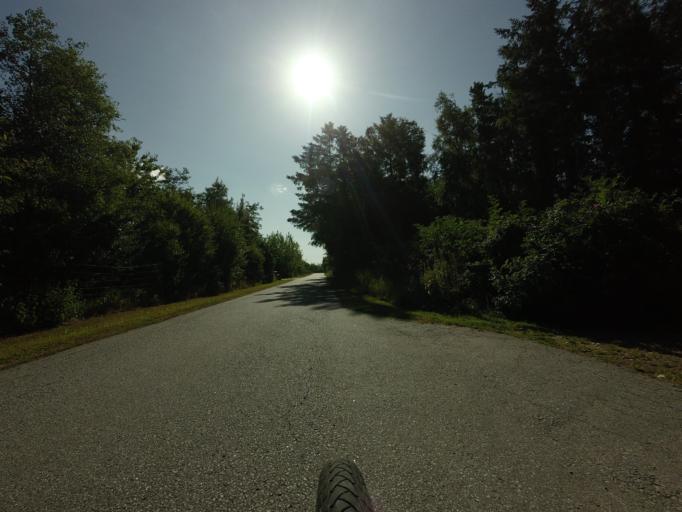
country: DK
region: North Denmark
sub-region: Hjorring Kommune
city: Vra
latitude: 57.3973
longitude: 9.9797
